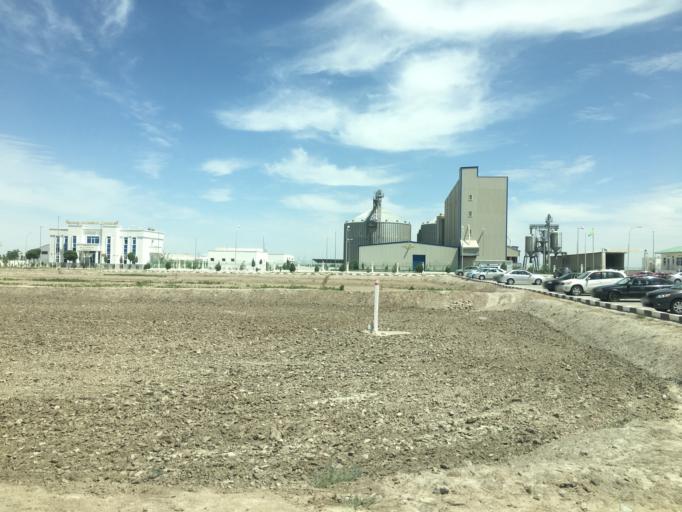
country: TM
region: Dasoguz
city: Tagta
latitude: 41.7231
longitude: 59.9416
